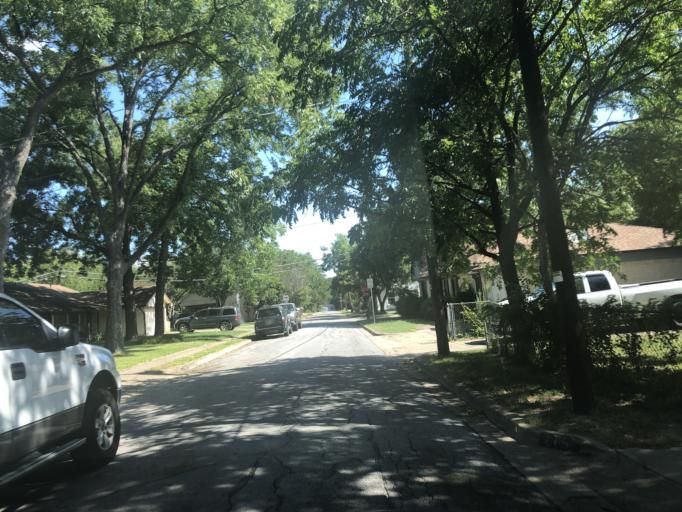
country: US
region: Texas
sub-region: Dallas County
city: Grand Prairie
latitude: 32.7475
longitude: -97.0020
